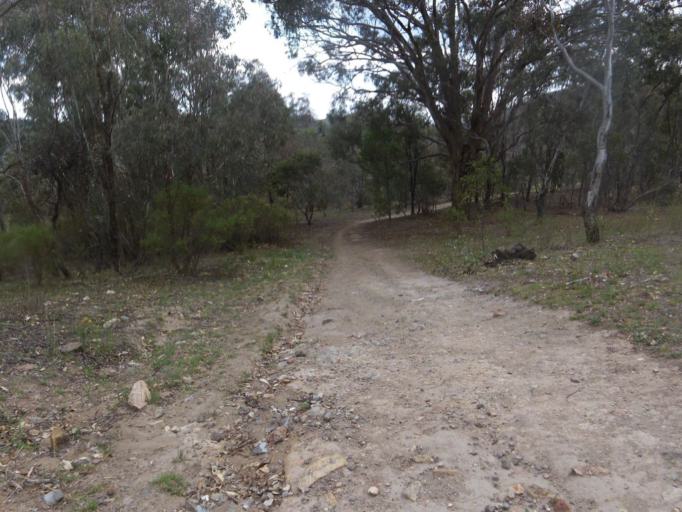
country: AU
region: Australian Capital Territory
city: Forrest
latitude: -35.3546
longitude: 149.1149
